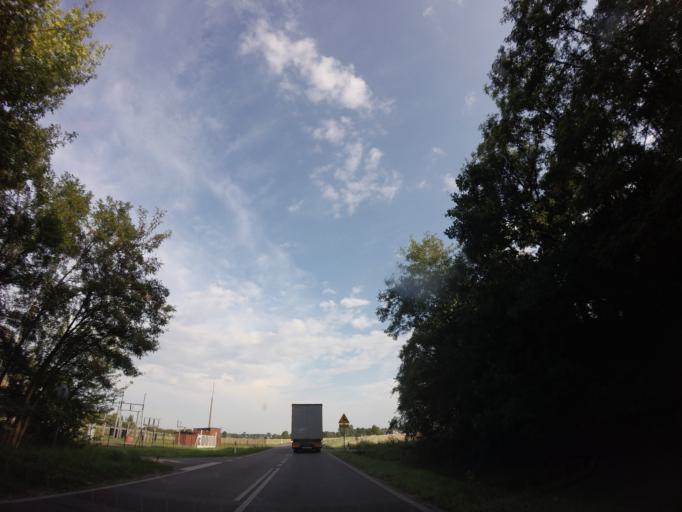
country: PL
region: Lublin Voivodeship
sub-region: Powiat lubartowski
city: Michow
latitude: 51.5353
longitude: 22.3104
